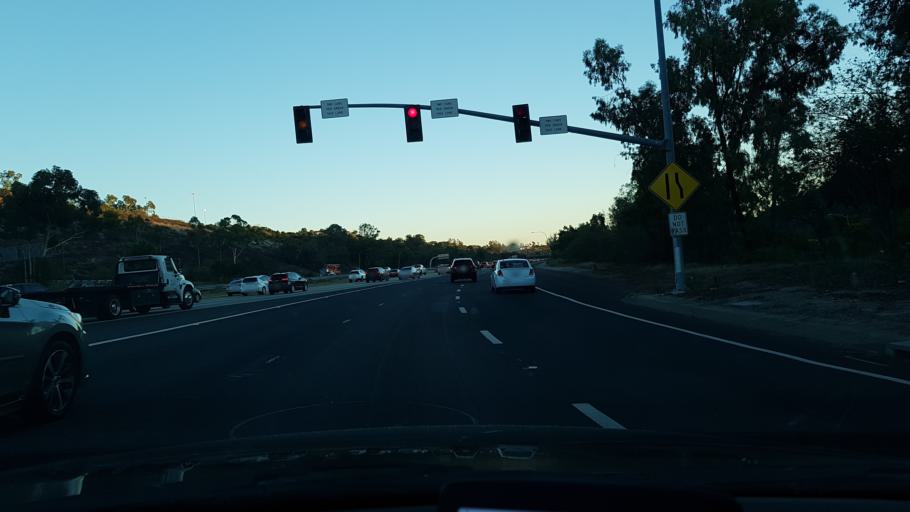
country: US
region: California
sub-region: San Diego County
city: La Mesa
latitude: 32.8210
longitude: -117.1166
